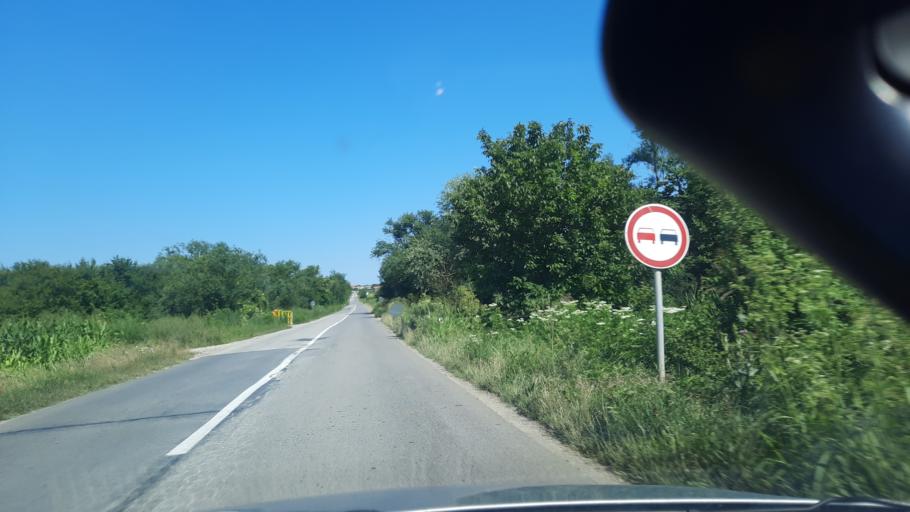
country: RS
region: Central Serbia
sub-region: Branicevski Okrug
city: Malo Crnice
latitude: 44.5764
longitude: 21.3414
